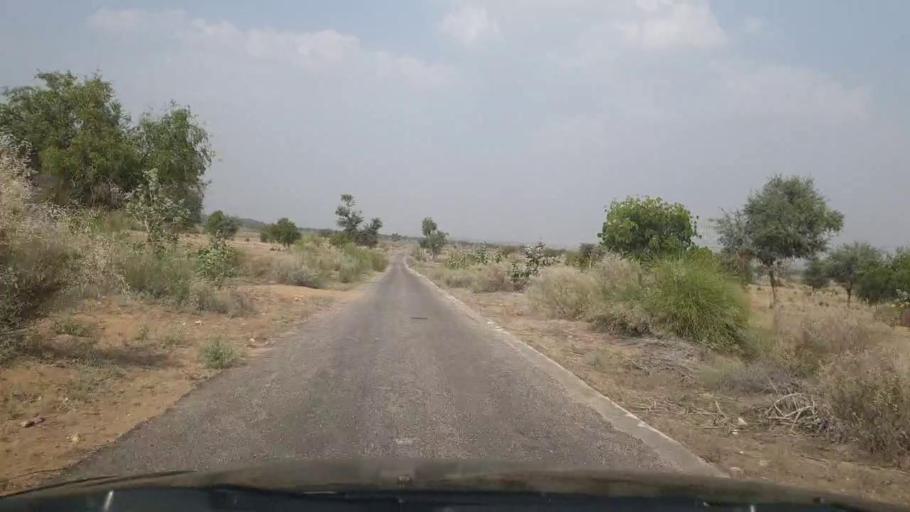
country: PK
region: Sindh
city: Islamkot
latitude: 24.8986
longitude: 70.5558
